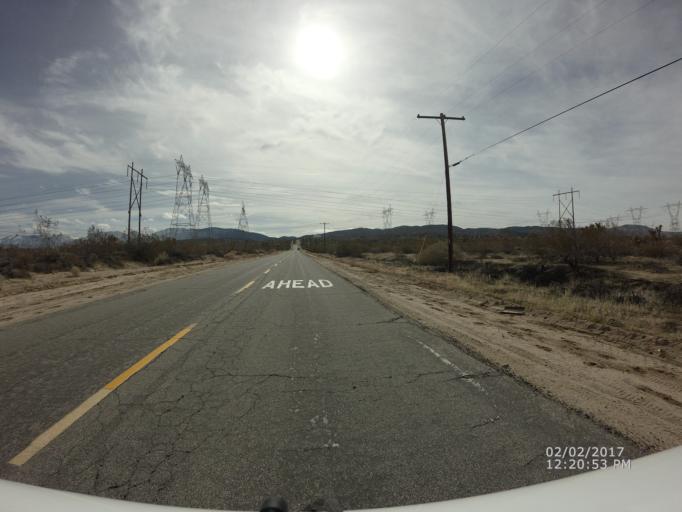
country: US
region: California
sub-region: Los Angeles County
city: Littlerock
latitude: 34.5125
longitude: -117.9749
